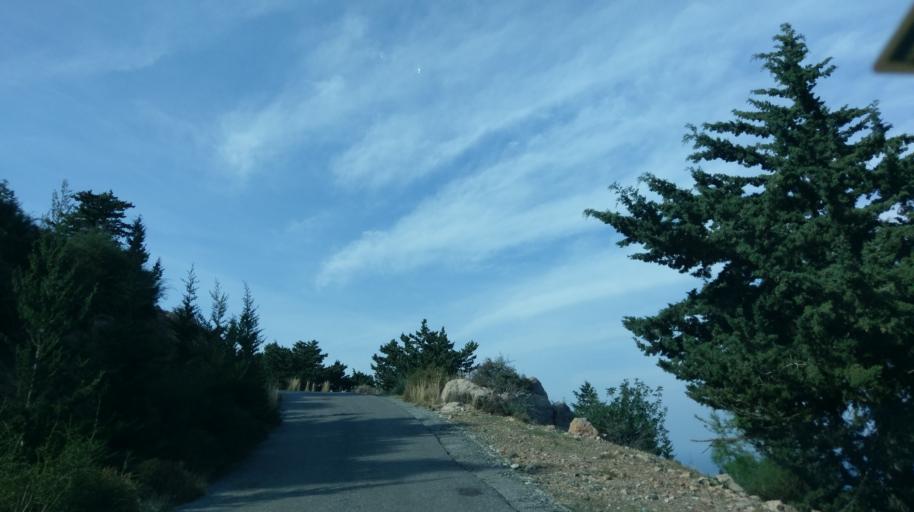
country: CY
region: Keryneia
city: Lapithos
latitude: 35.3395
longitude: 33.1138
